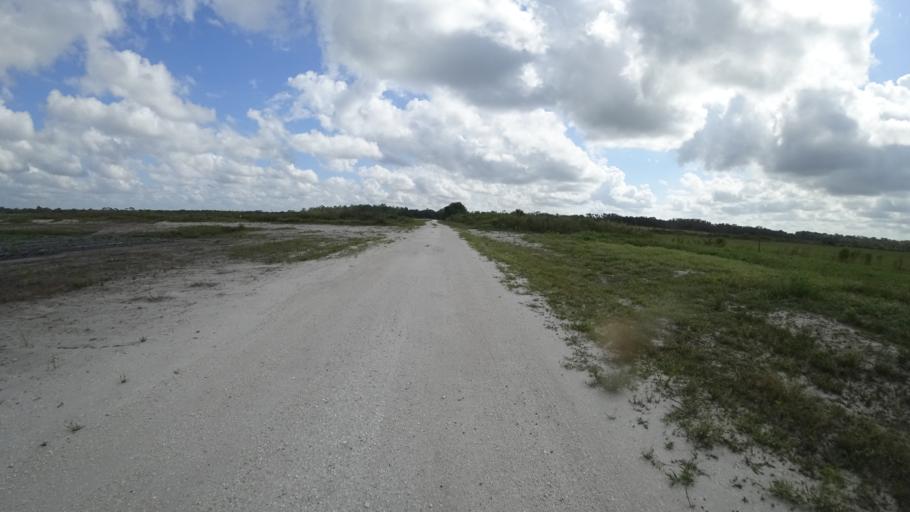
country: US
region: Florida
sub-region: Sarasota County
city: Lake Sarasota
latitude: 27.4034
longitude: -82.2041
